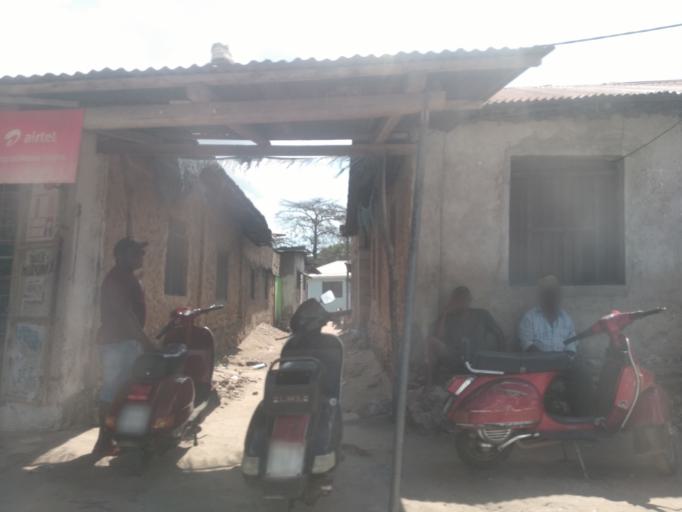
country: TZ
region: Zanzibar Urban/West
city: Zanzibar
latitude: -6.1701
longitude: 39.2102
